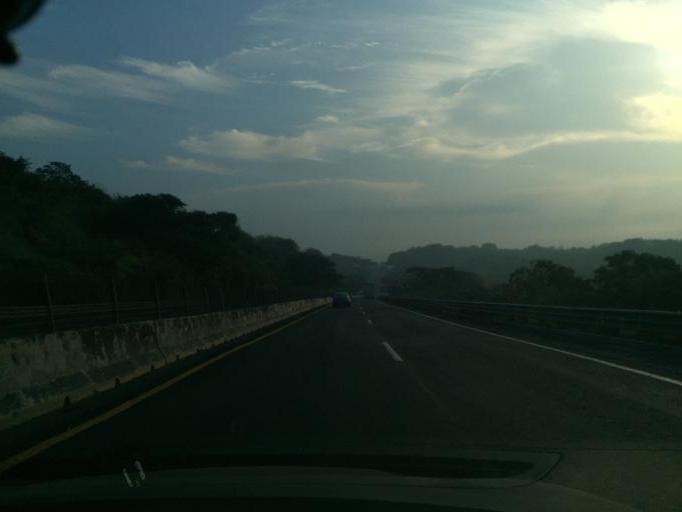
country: MX
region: Veracruz
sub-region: Tierra Blanca
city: Huixcolotla
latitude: 18.7822
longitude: -96.4764
